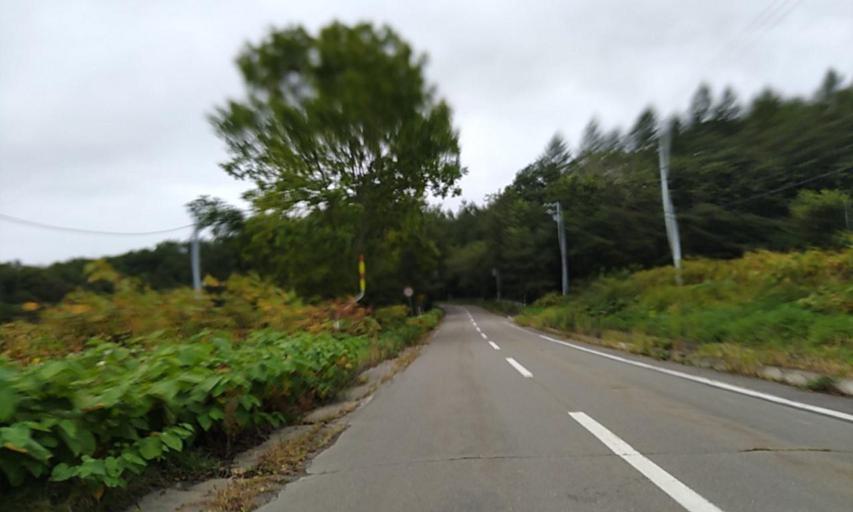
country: JP
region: Hokkaido
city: Obihiro
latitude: 42.6721
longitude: 143.0437
